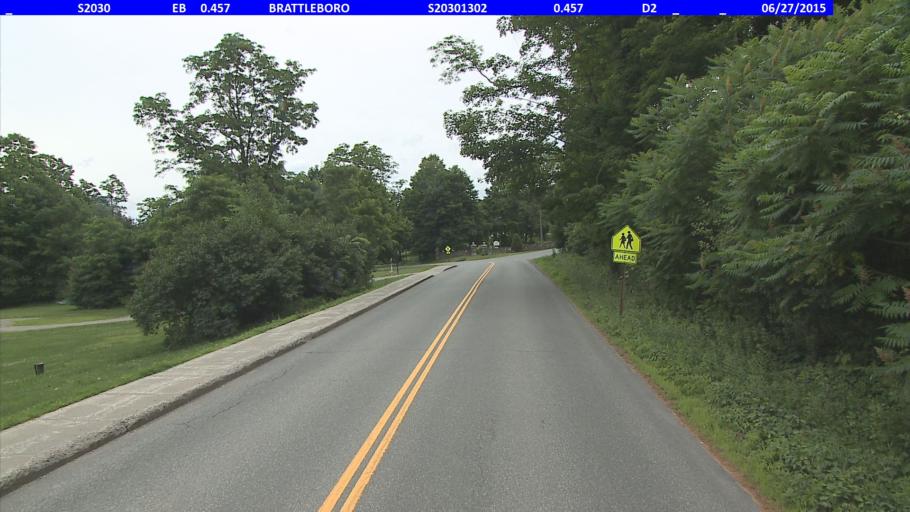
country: US
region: Vermont
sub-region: Windham County
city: Brattleboro
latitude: 42.8453
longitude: -72.5751
